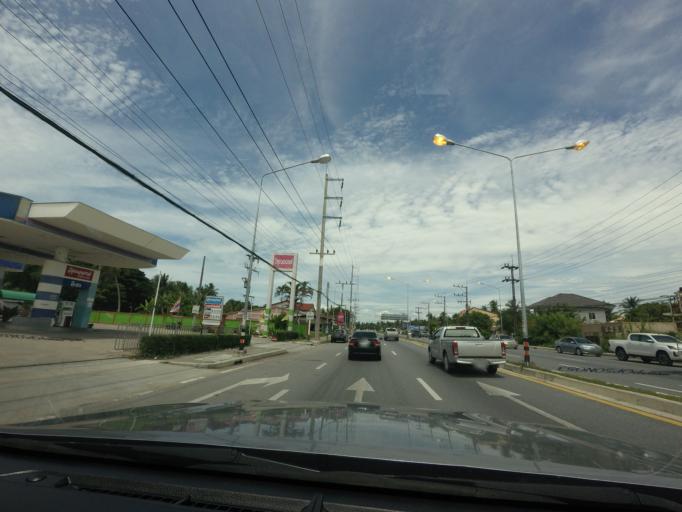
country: TH
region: Songkhla
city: Krasae Sin
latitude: 7.6013
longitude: 100.4011
